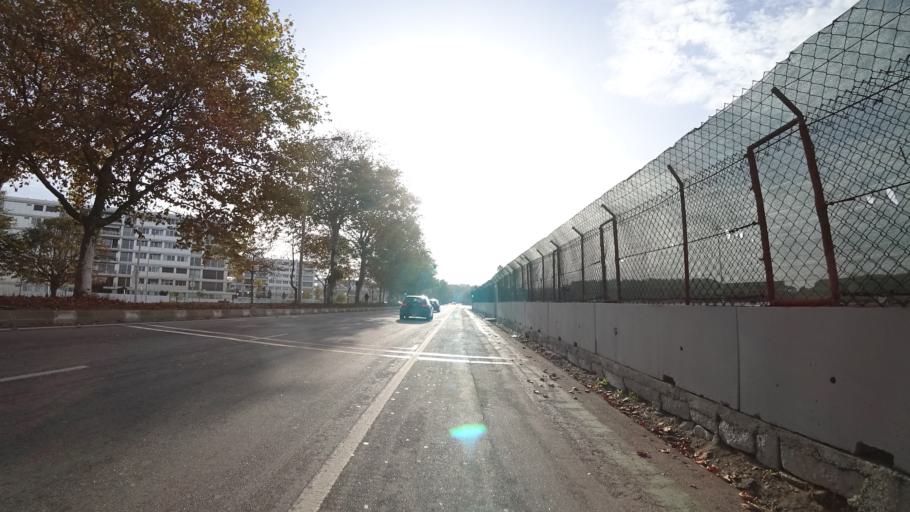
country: PT
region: Porto
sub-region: Matosinhos
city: Matosinhos
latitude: 41.1734
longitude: -8.6836
